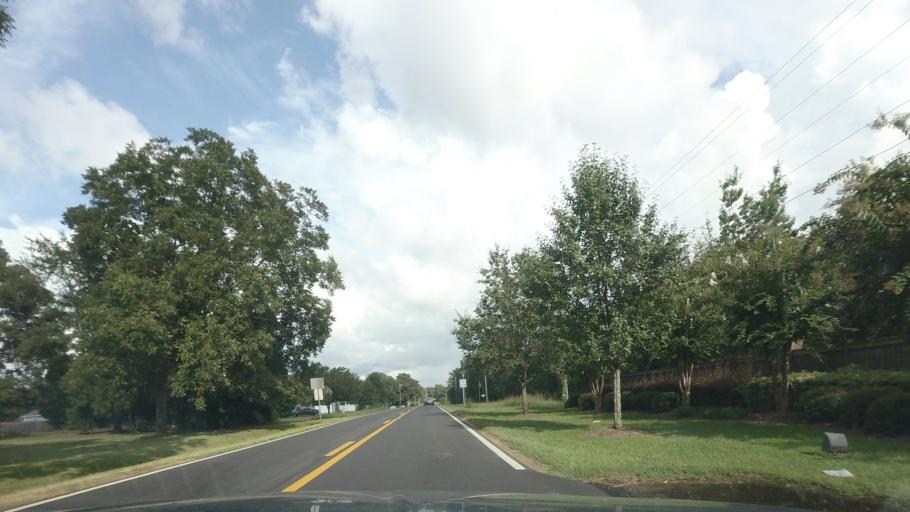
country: US
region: Georgia
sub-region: Houston County
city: Centerville
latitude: 32.6350
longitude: -83.7188
